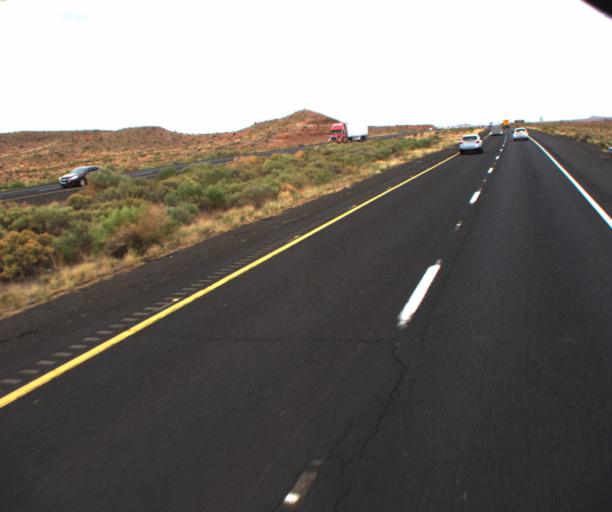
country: US
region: Arizona
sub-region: Navajo County
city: Joseph City
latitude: 34.9173
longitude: -110.2527
